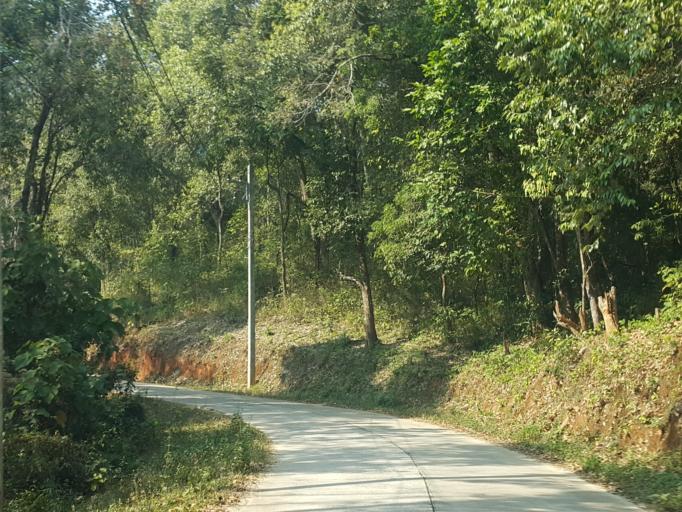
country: TH
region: Chiang Mai
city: Samoeng
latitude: 19.0269
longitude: 98.7746
